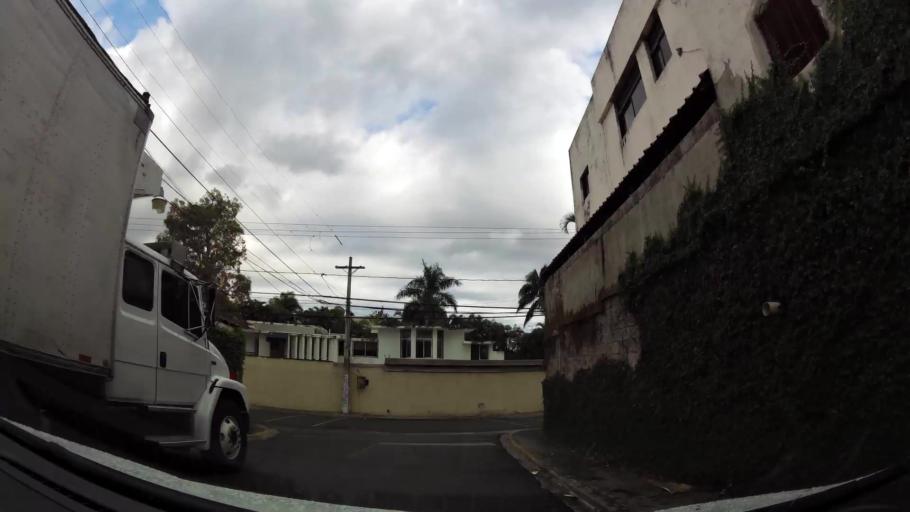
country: DO
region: Nacional
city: La Agustina
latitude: 18.4983
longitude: -69.9362
